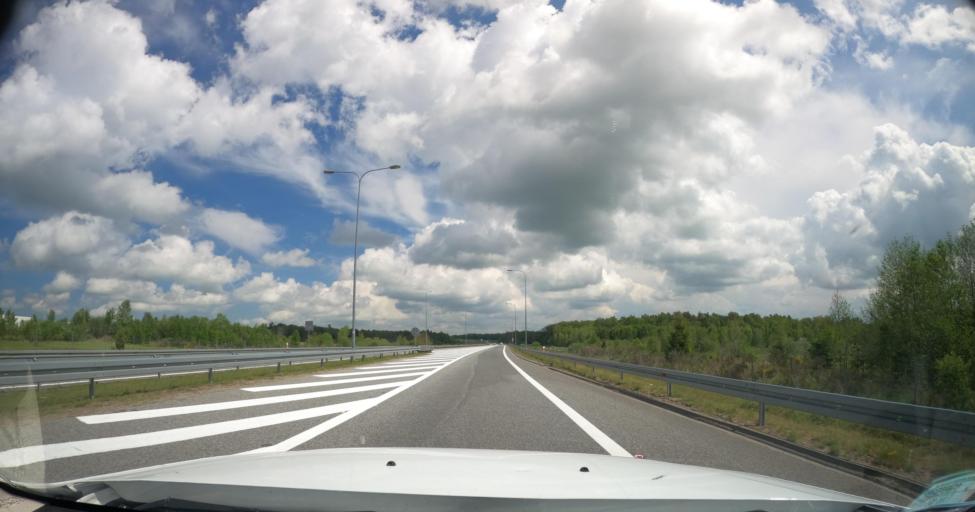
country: PL
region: Pomeranian Voivodeship
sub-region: Slupsk
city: Slupsk
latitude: 54.4557
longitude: 17.0914
